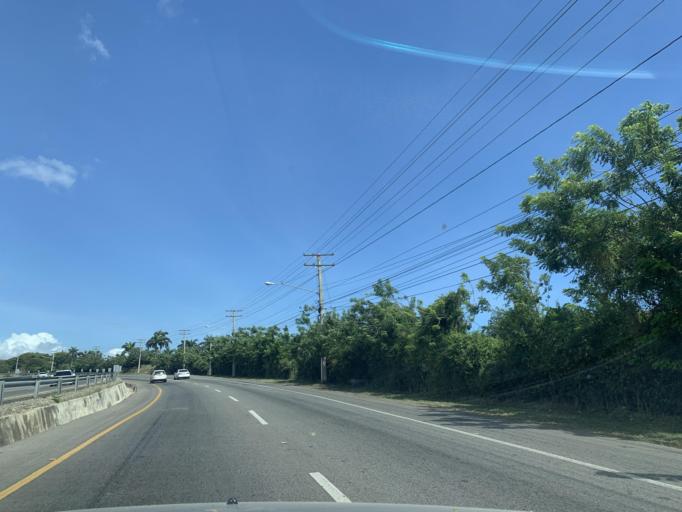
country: DO
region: Puerto Plata
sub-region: Puerto Plata
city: Puerto Plata
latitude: 19.8276
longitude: -70.7500
